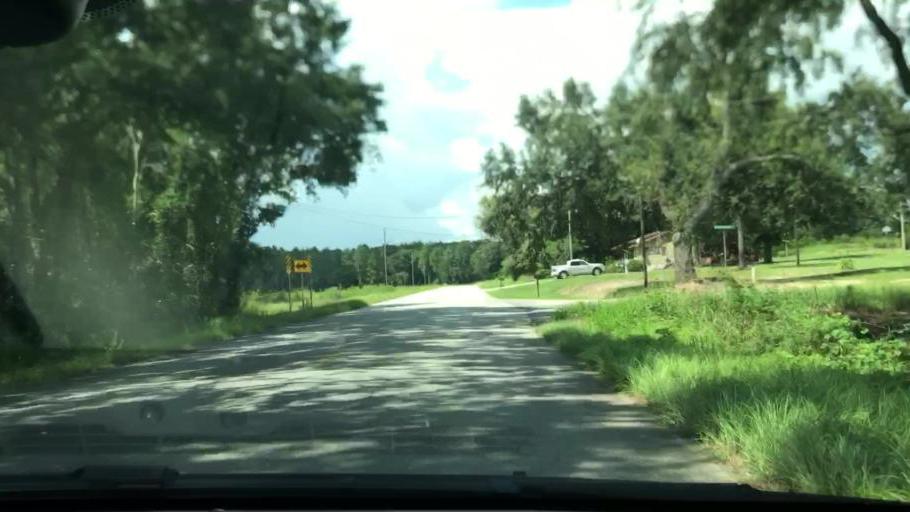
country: US
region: Georgia
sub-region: Seminole County
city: Donalsonville
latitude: 30.9892
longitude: -84.9785
